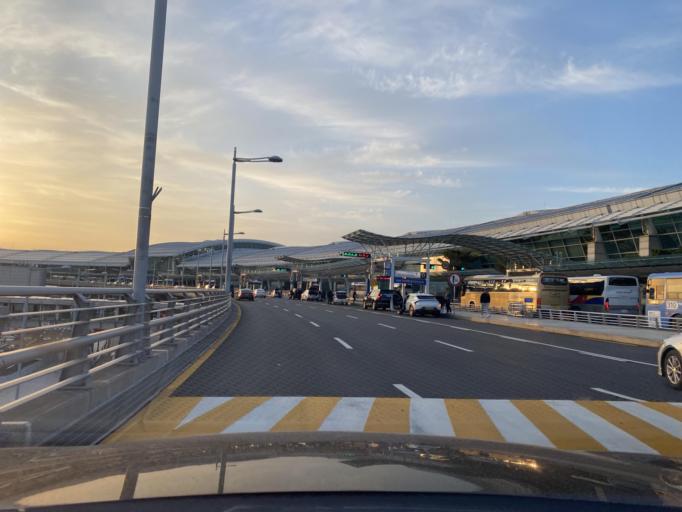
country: KR
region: Incheon
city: Incheon
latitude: 37.4491
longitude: 126.4546
